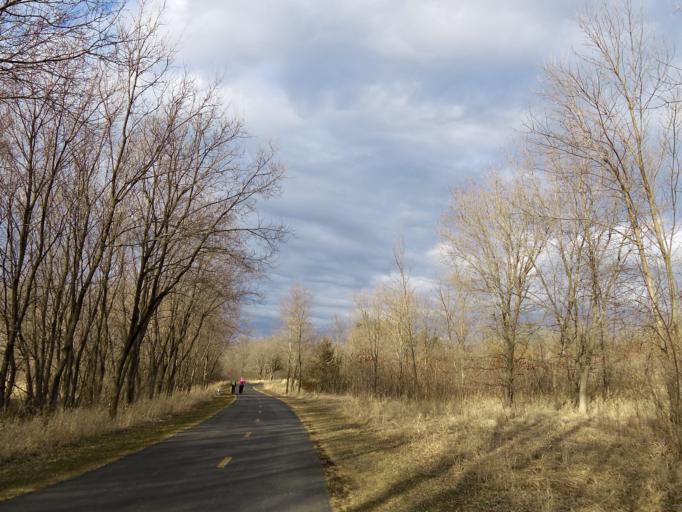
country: US
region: Minnesota
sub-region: Scott County
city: Prior Lake
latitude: 44.6918
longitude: -93.3820
